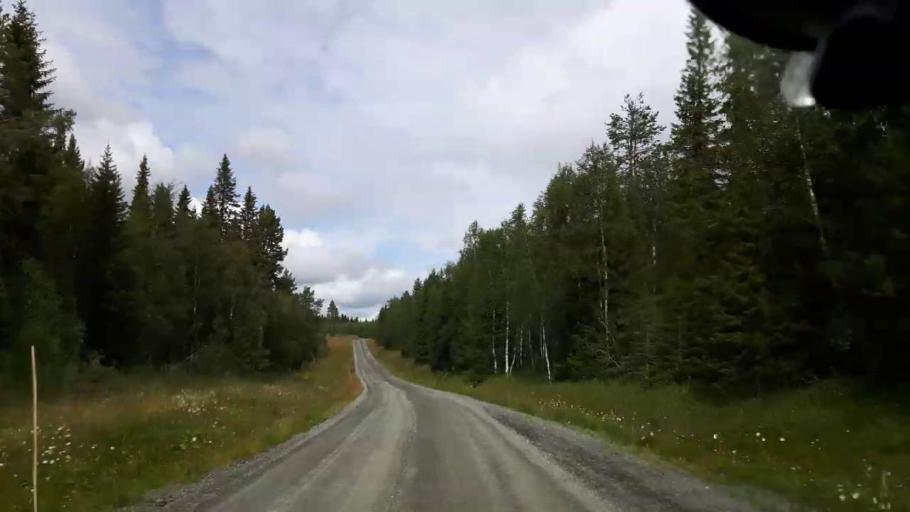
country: SE
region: Jaemtland
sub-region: Krokoms Kommun
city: Valla
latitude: 63.5490
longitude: 13.9166
